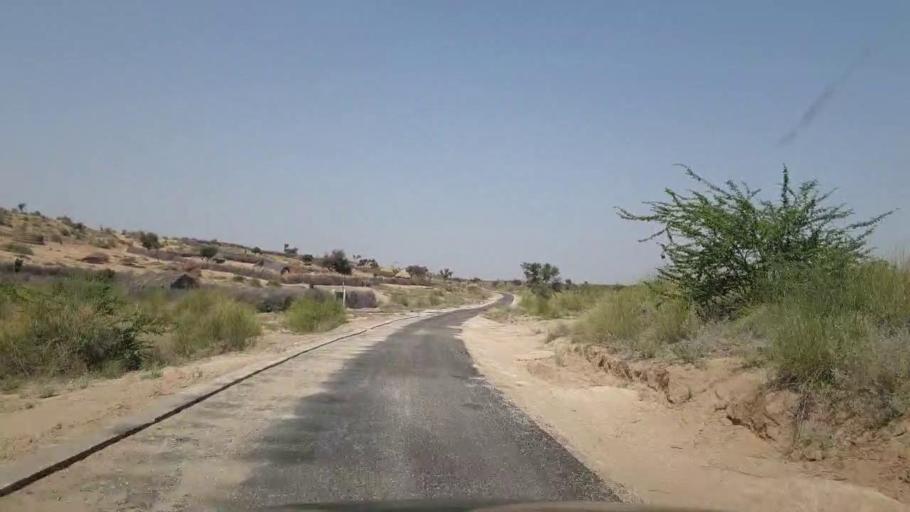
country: PK
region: Sindh
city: Islamkot
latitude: 25.1143
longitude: 70.6512
